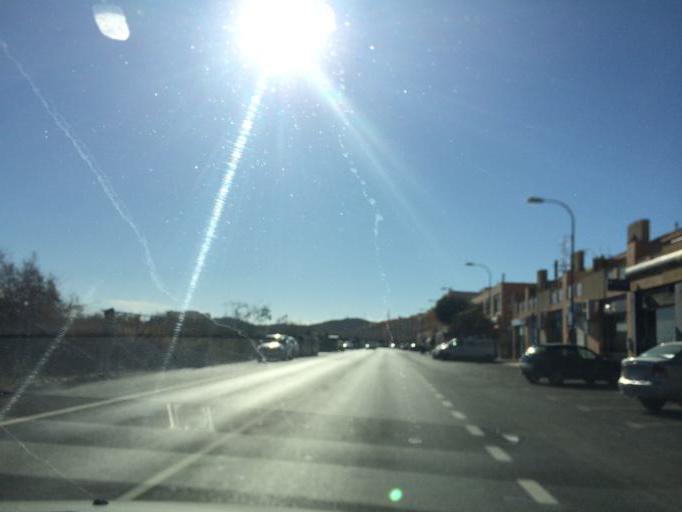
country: ES
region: Andalusia
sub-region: Provincia de Almeria
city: Huercal de Almeria
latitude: 36.8777
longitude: -2.4388
